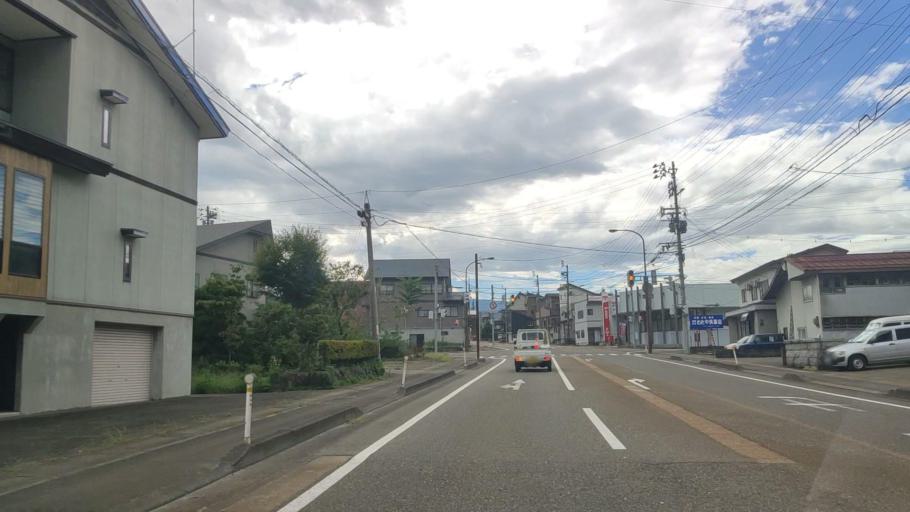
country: JP
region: Niigata
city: Arai
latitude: 36.9879
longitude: 138.2716
